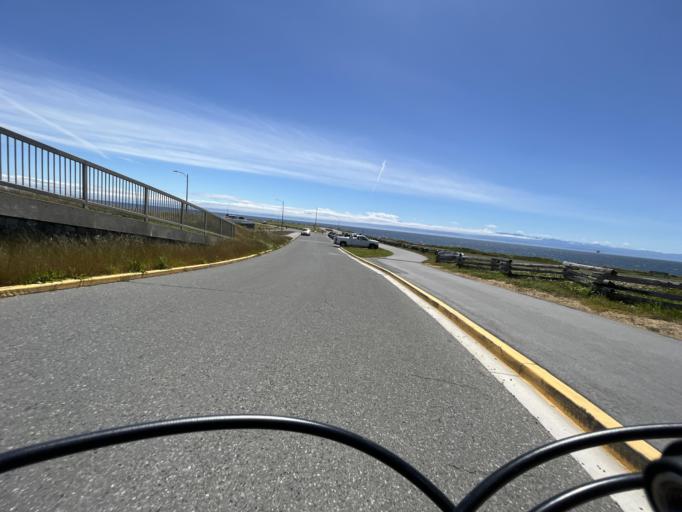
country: CA
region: British Columbia
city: Victoria
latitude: 48.4053
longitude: -123.3497
